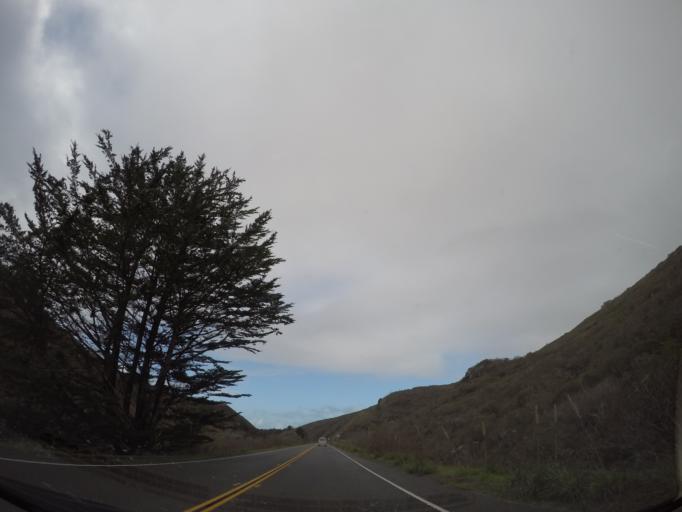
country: US
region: California
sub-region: Sonoma County
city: Bodega Bay
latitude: 38.3185
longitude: -123.0189
